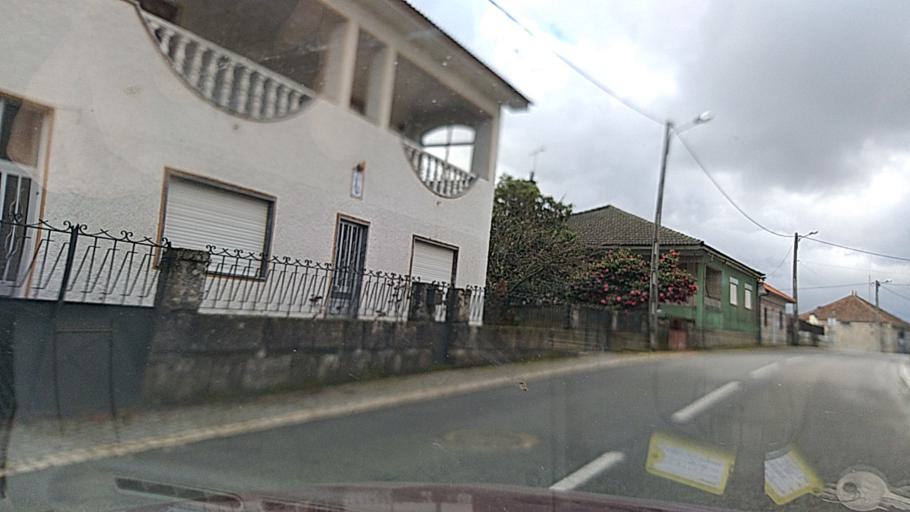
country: PT
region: Guarda
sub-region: Fornos de Algodres
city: Fornos de Algodres
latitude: 40.6576
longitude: -7.5806
